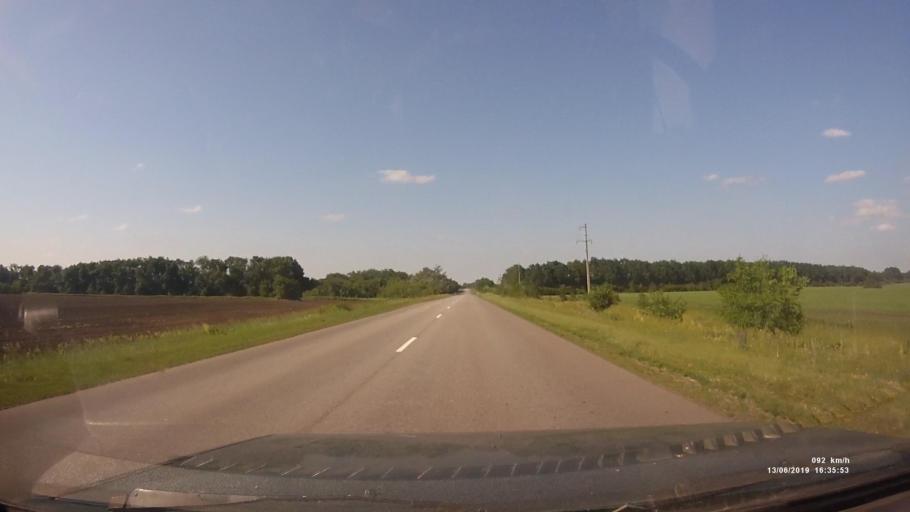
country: RU
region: Rostov
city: Kazanskaya
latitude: 49.8878
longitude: 41.3017
